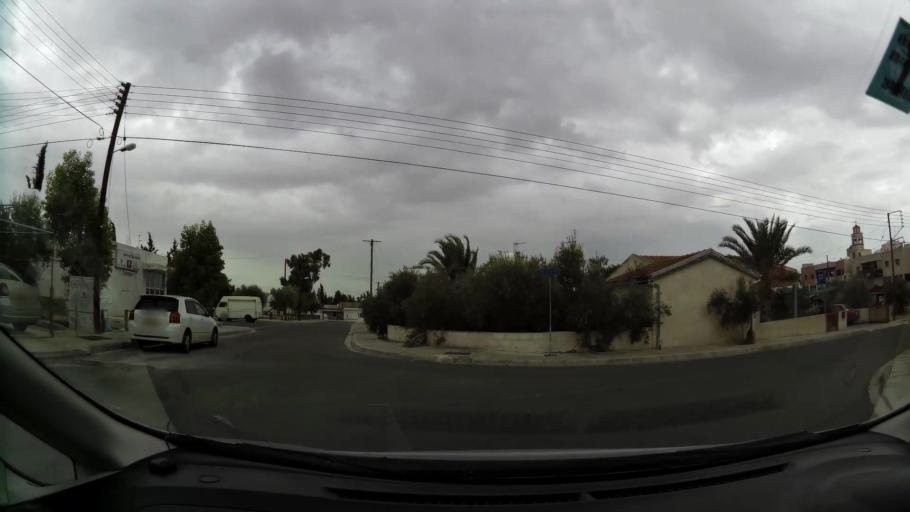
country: CY
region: Lefkosia
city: Geri
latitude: 35.1051
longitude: 33.3875
